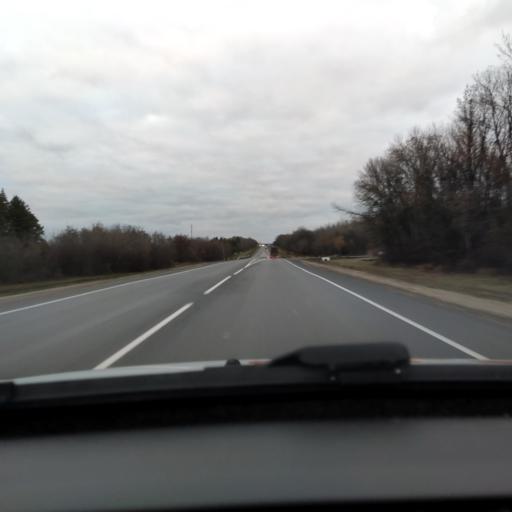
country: RU
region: Lipetsk
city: Khlevnoye
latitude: 52.2439
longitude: 39.1513
